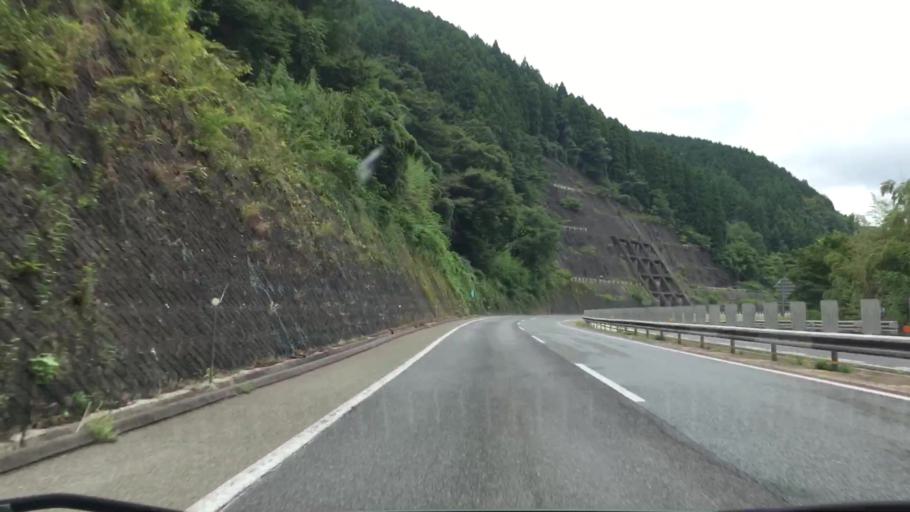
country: JP
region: Hiroshima
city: Shobara
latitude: 34.8971
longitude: 133.2377
